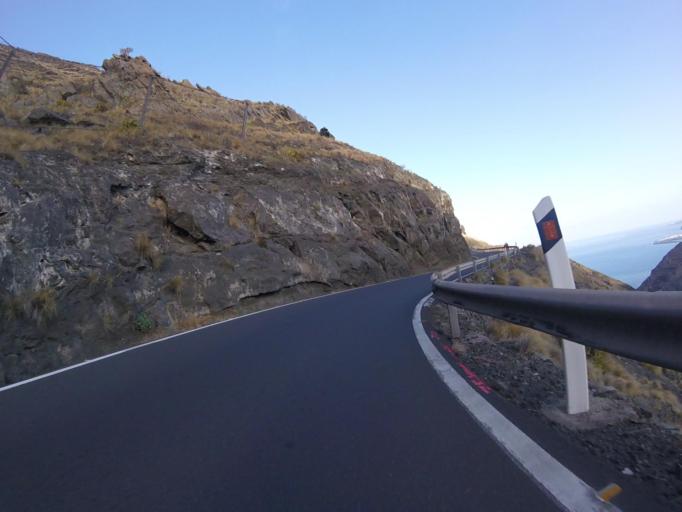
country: ES
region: Canary Islands
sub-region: Provincia de Las Palmas
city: Agaete
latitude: 28.0719
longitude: -15.7132
